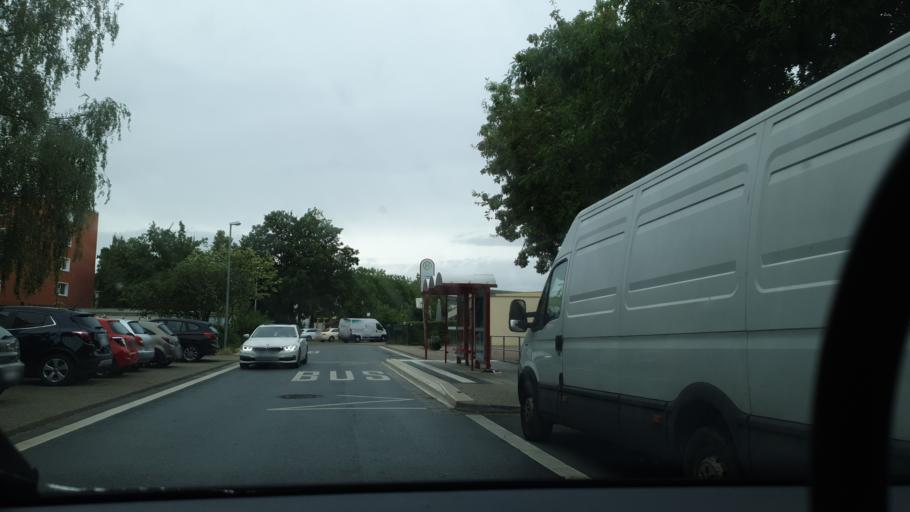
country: DE
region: Hesse
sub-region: Regierungsbezirk Darmstadt
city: Hofheim am Taunus
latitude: 50.0760
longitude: 8.4451
